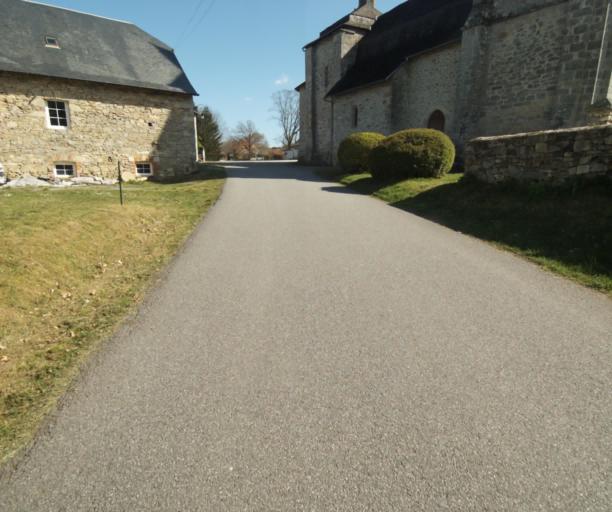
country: FR
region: Limousin
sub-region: Departement de la Correze
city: Saint-Mexant
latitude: 45.2853
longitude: 1.6550
